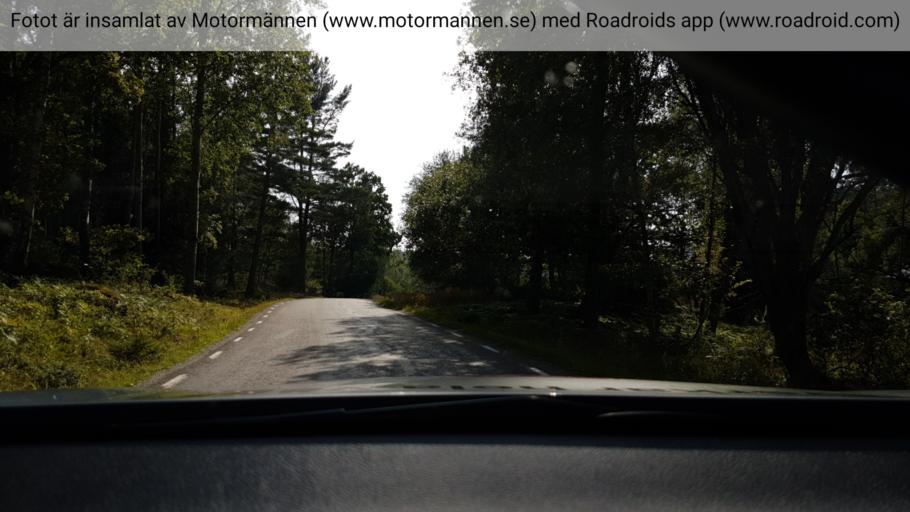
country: SE
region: Stockholm
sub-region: Nynashamns Kommun
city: Osmo
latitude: 58.8856
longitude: 17.7871
